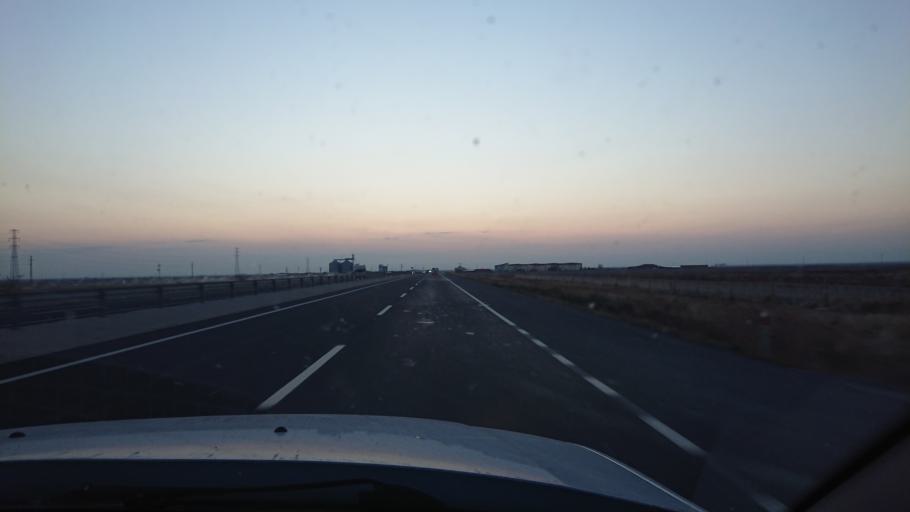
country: TR
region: Aksaray
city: Yesilova
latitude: 38.3119
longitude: 33.8301
